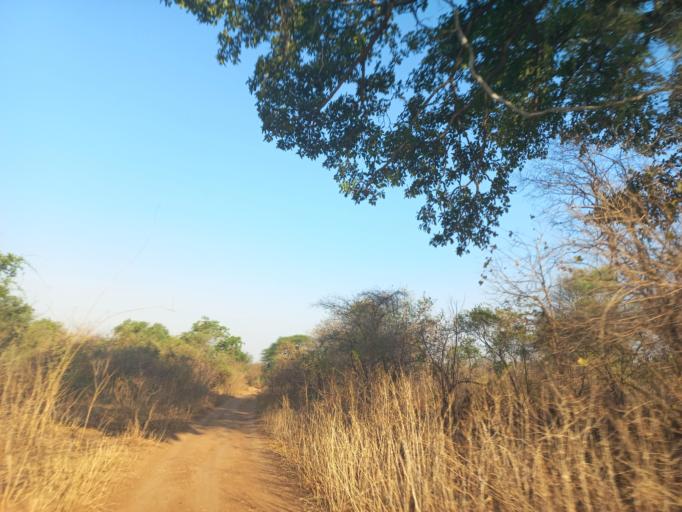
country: ZM
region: Lusaka
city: Luangwa
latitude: -15.4214
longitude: 30.2743
